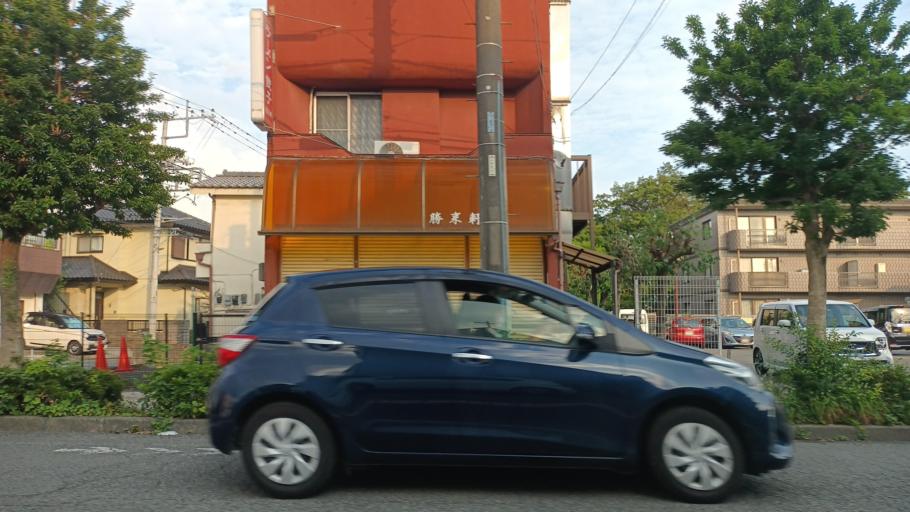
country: JP
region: Tokyo
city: Fussa
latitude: 35.7612
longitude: 139.3194
